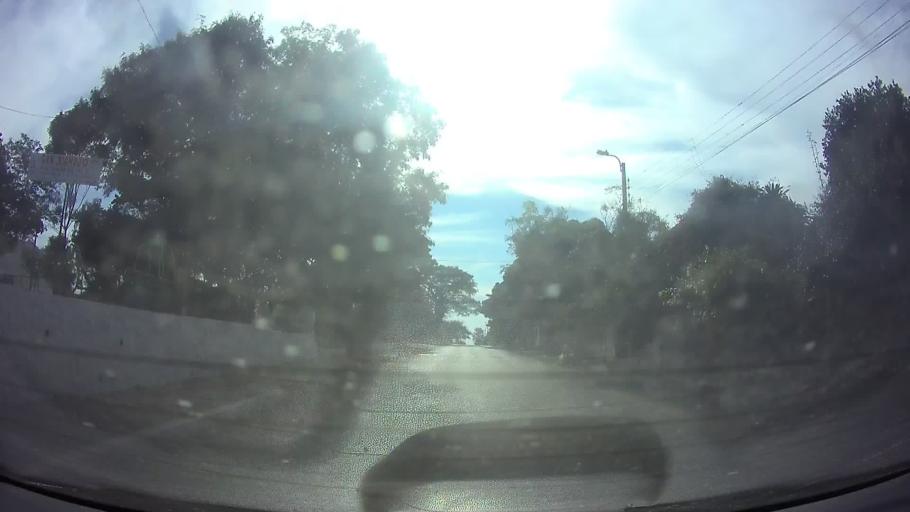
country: PY
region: Central
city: Villa Elisa
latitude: -25.3388
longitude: -57.5671
